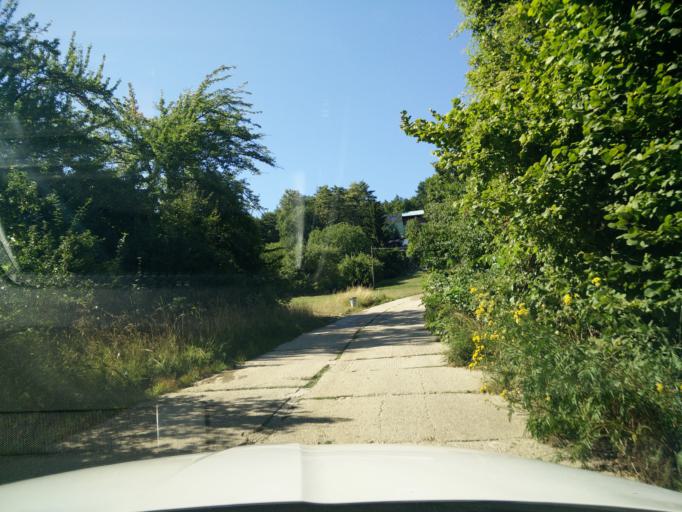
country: SK
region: Nitriansky
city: Bojnice
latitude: 48.7882
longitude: 18.5755
